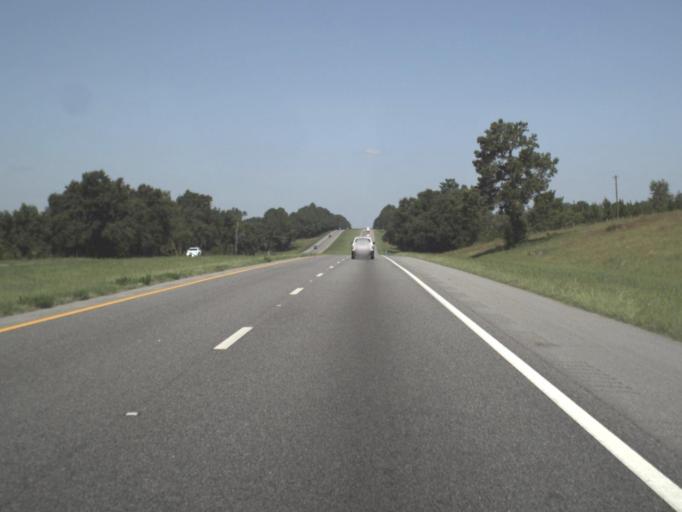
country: US
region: Florida
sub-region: Suwannee County
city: Live Oak
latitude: 30.3494
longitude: -82.9995
